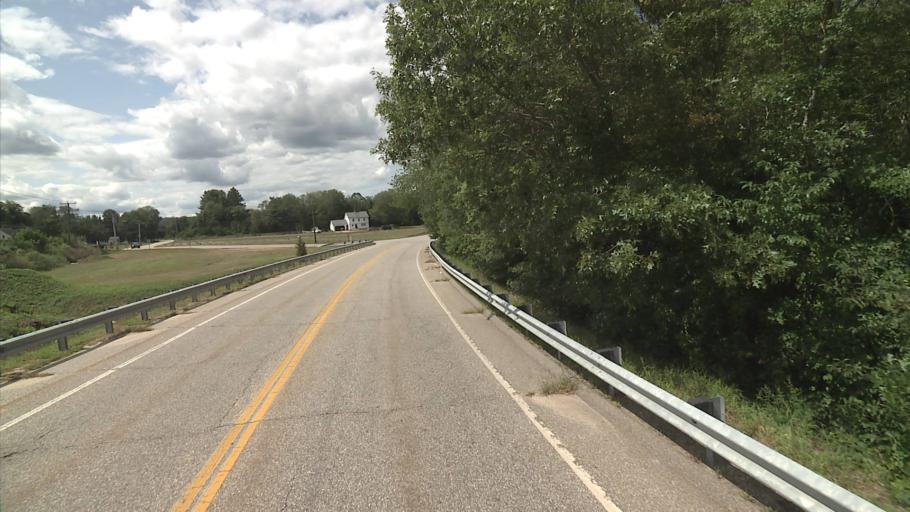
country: US
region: Connecticut
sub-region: New London County
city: Baltic
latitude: 41.6179
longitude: -72.1154
